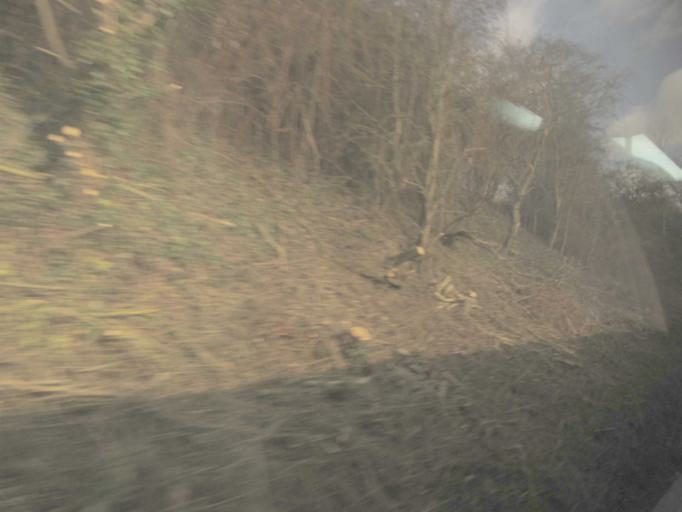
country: GB
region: England
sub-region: Royal Borough of Windsor and Maidenhead
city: White Waltham
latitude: 51.4927
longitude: -0.8102
